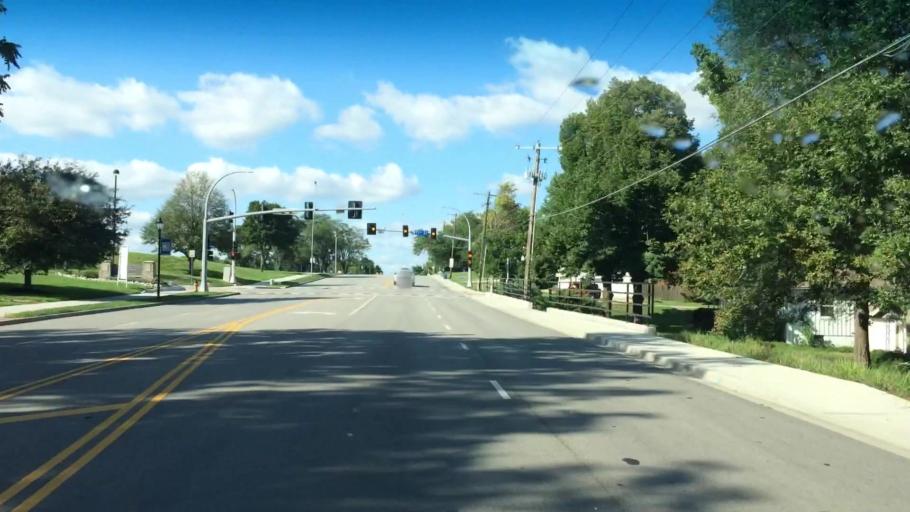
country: US
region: Kansas
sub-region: Johnson County
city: Prairie Village
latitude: 38.9889
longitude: -94.6304
